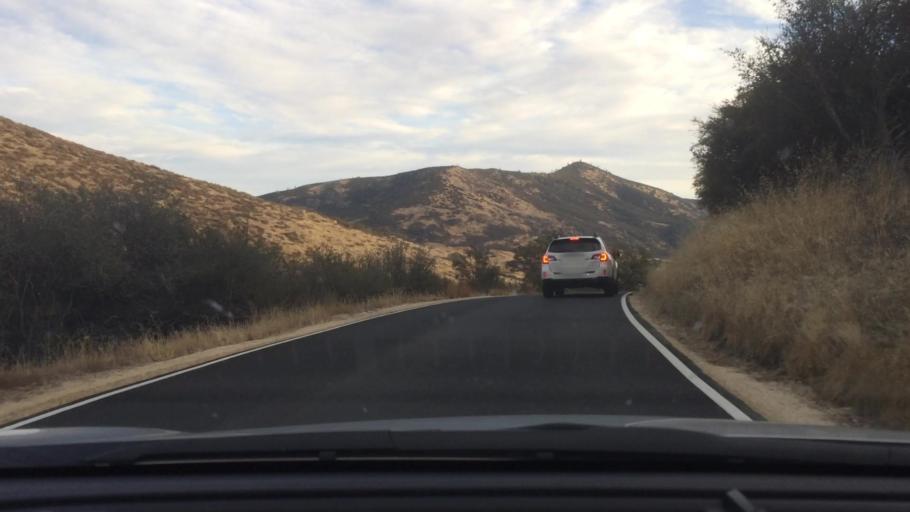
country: US
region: California
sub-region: Monterey County
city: Soledad
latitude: 36.4723
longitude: -121.2232
